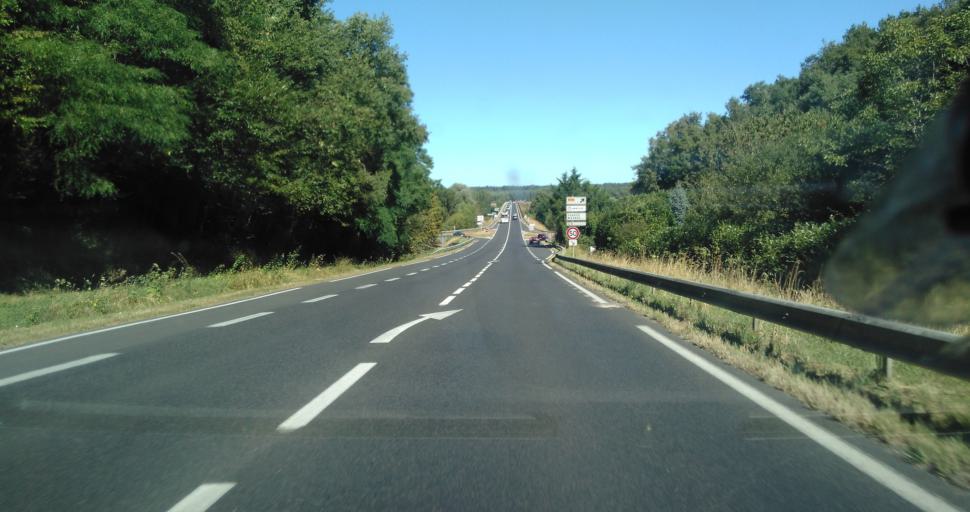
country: FR
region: Centre
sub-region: Departement d'Indre-et-Loire
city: Charge
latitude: 47.4225
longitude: 1.0133
